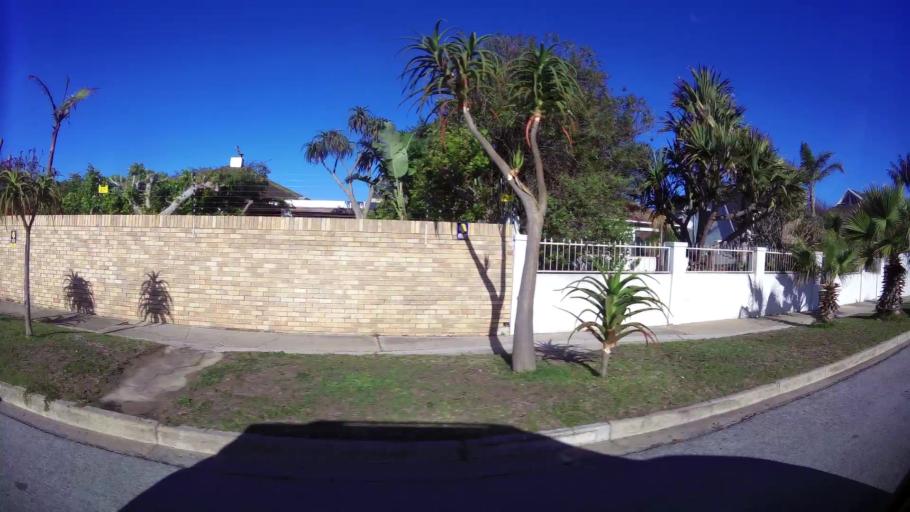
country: ZA
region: Eastern Cape
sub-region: Nelson Mandela Bay Metropolitan Municipality
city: Port Elizabeth
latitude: -33.9866
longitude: 25.6649
